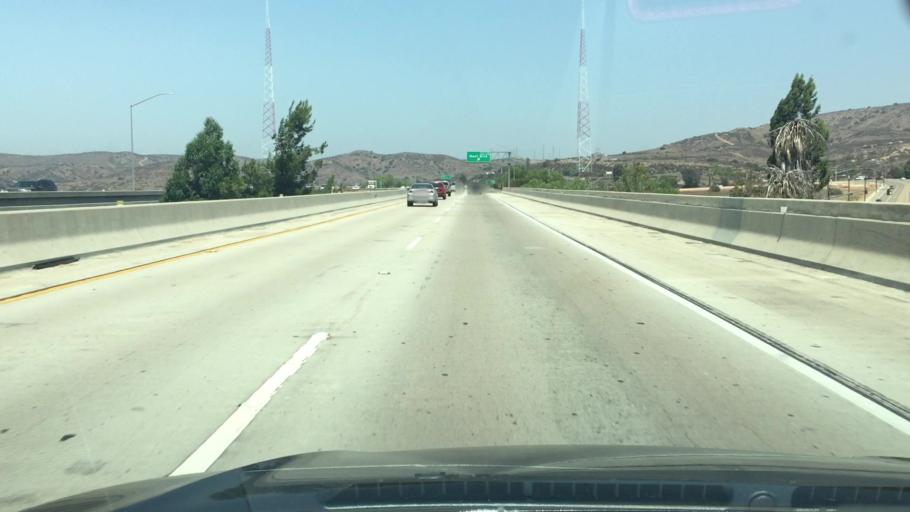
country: US
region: California
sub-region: San Diego County
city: Santee
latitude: 32.8401
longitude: -117.0235
